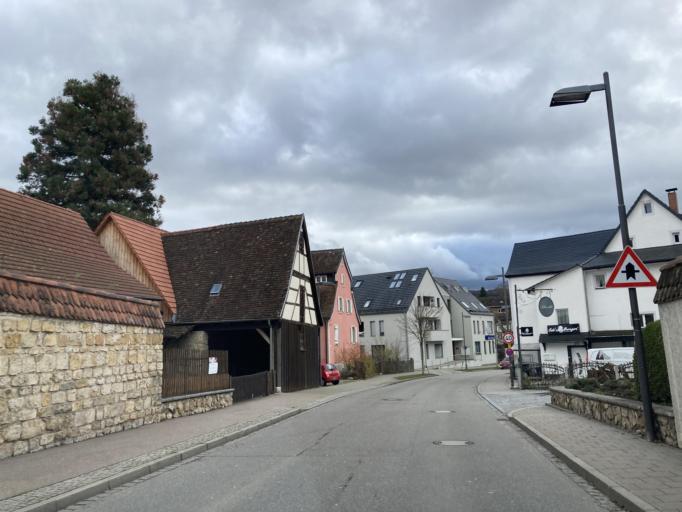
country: DE
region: Baden-Wuerttemberg
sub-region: Freiburg Region
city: Mullheim
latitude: 47.8074
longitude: 7.6312
